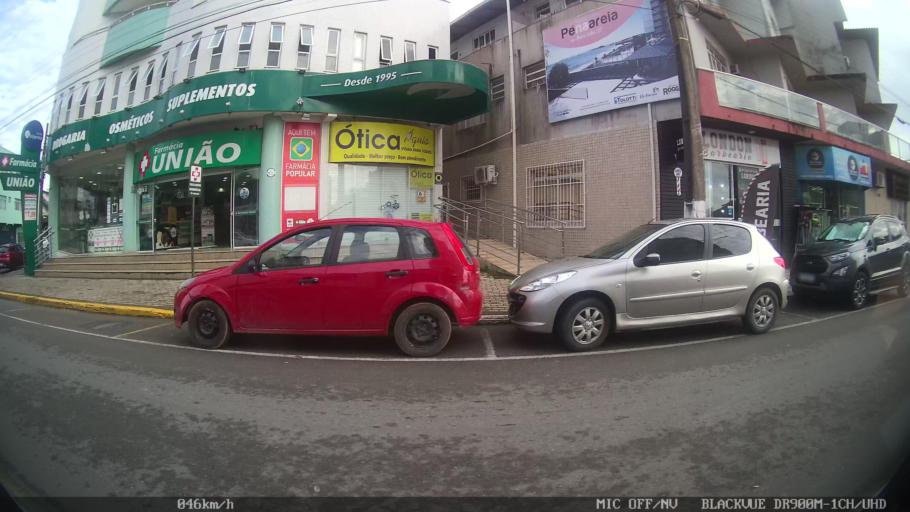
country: BR
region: Santa Catarina
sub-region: Barra Velha
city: Barra Velha
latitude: -26.6428
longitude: -48.6846
